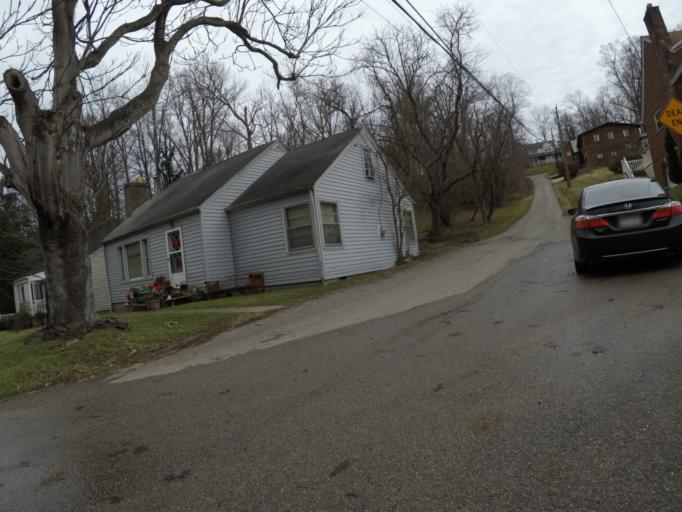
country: US
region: Ohio
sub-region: Lawrence County
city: Burlington
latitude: 38.3910
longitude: -82.5149
